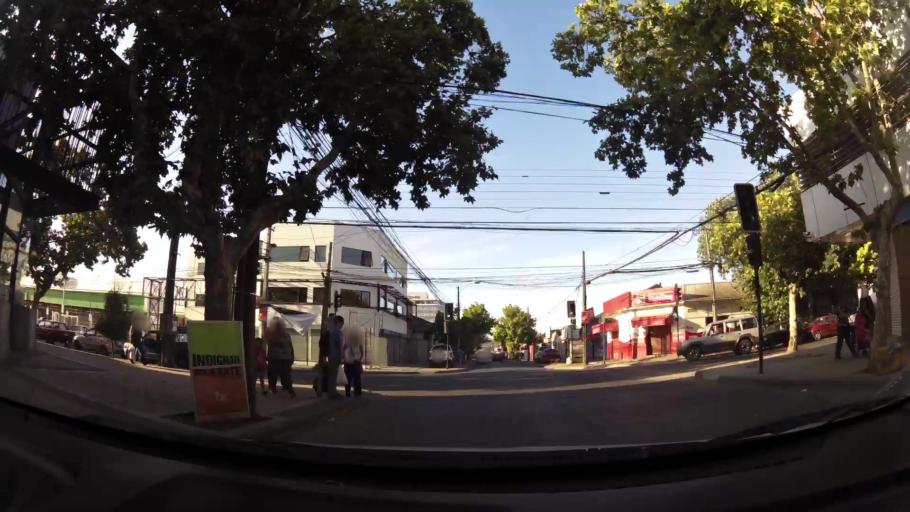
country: CL
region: Maule
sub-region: Provincia de Talca
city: Talca
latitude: -35.4300
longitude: -71.6454
